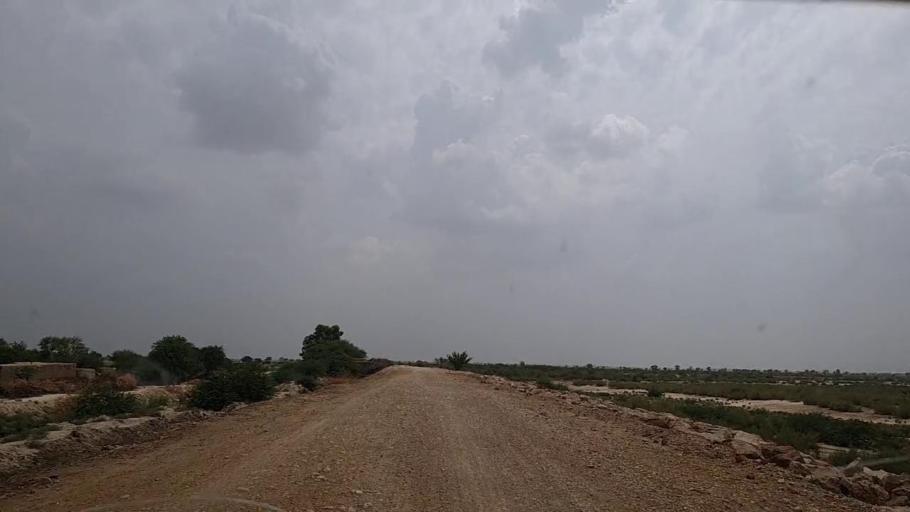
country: PK
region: Sindh
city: Johi
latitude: 26.7336
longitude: 67.5802
